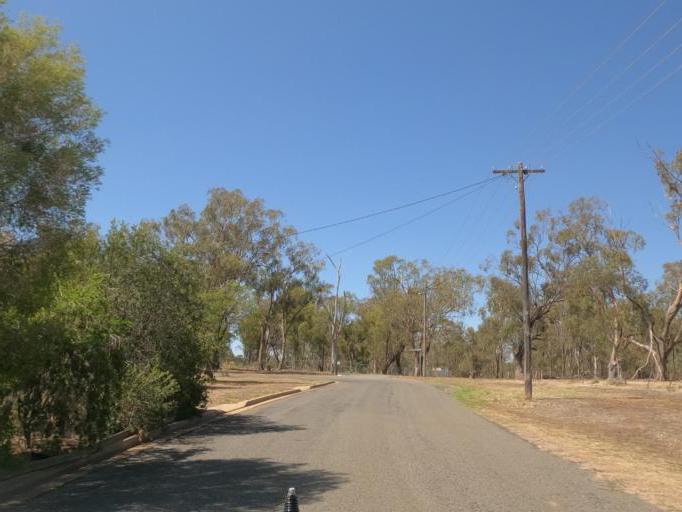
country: AU
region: New South Wales
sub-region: Corowa Shire
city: Mulwala
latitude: -35.9953
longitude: 145.9950
